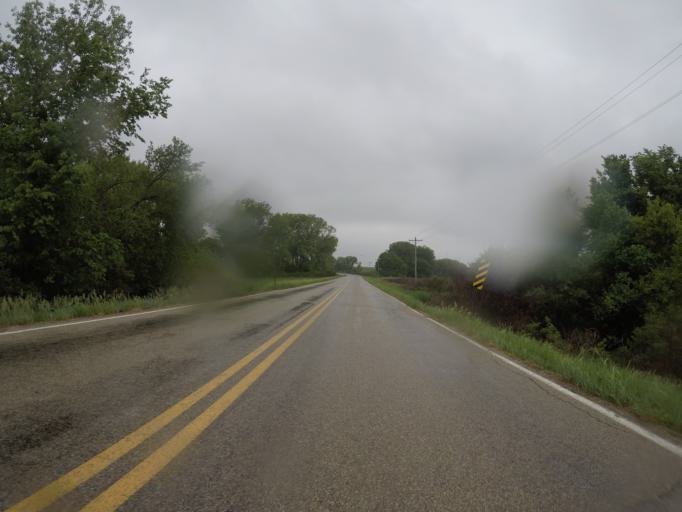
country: US
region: Kansas
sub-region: Pottawatomie County
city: Wamego
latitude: 39.3840
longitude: -96.2036
